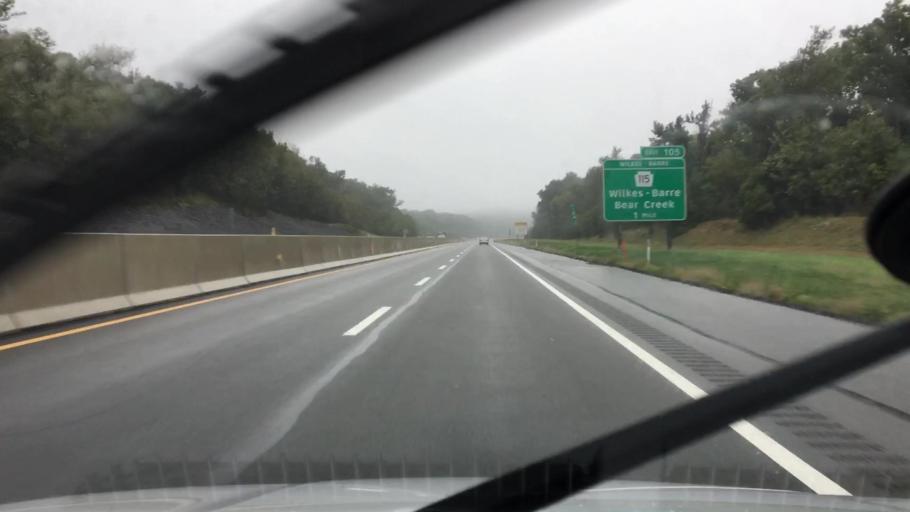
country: US
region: Pennsylvania
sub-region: Luzerne County
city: Mountain Top
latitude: 41.1814
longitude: -75.7862
